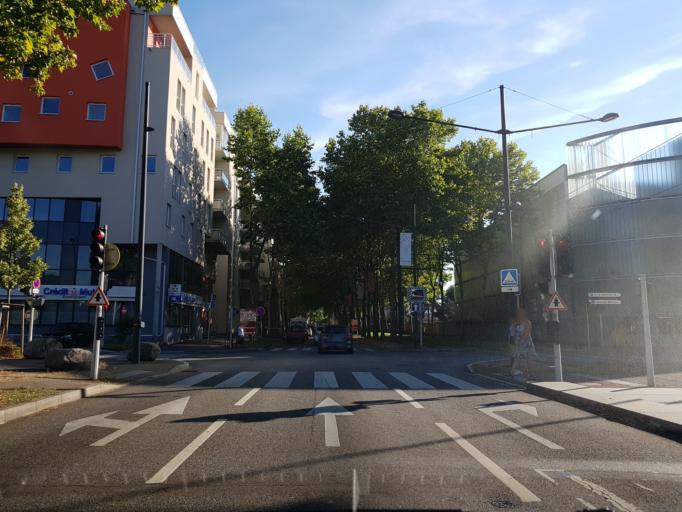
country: FR
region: Alsace
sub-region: Departement du Haut-Rhin
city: Riedisheim
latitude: 47.7595
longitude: 7.3511
